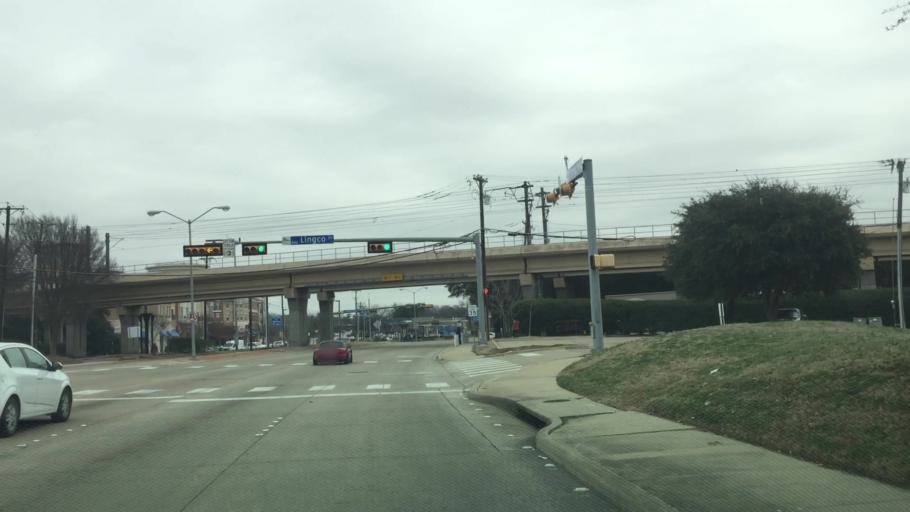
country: US
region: Texas
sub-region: Dallas County
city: Richardson
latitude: 32.9400
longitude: -96.7389
